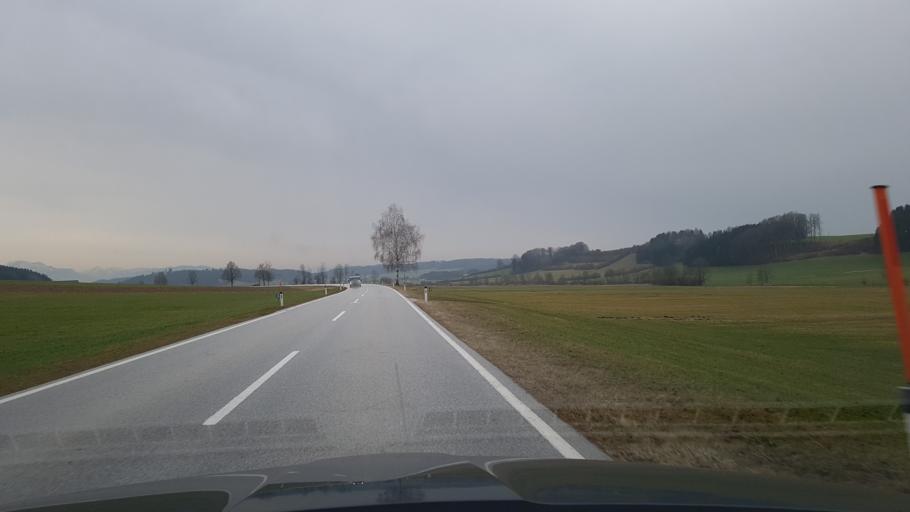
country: AT
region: Salzburg
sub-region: Politischer Bezirk Salzburg-Umgebung
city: Dorfbeuern
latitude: 47.9964
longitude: 13.0265
